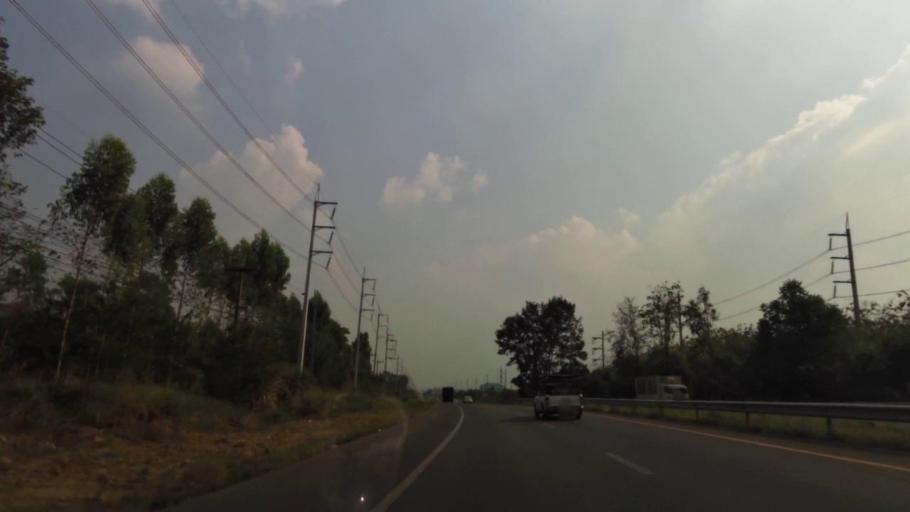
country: TH
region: Chon Buri
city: Nong Yai
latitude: 13.1931
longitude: 101.2465
